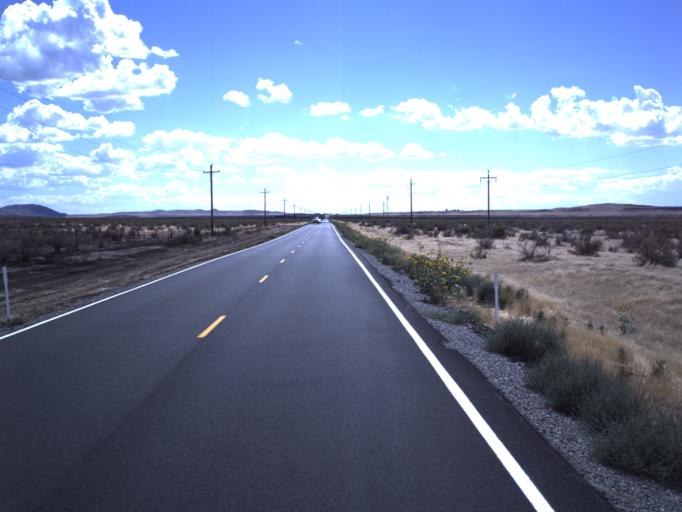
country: US
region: Utah
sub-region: Tooele County
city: Grantsville
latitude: 40.2698
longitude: -112.6823
